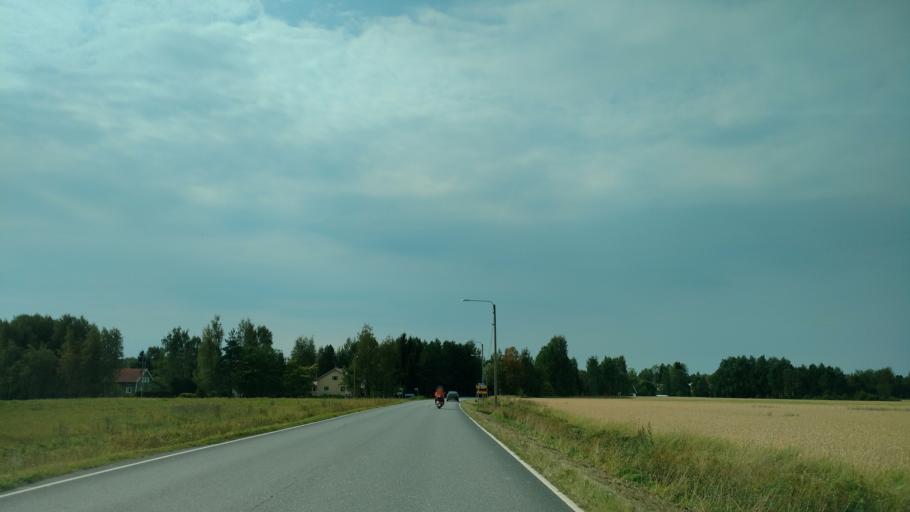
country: FI
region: Varsinais-Suomi
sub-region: Loimaa
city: Koski Tl
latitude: 60.6637
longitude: 23.1519
